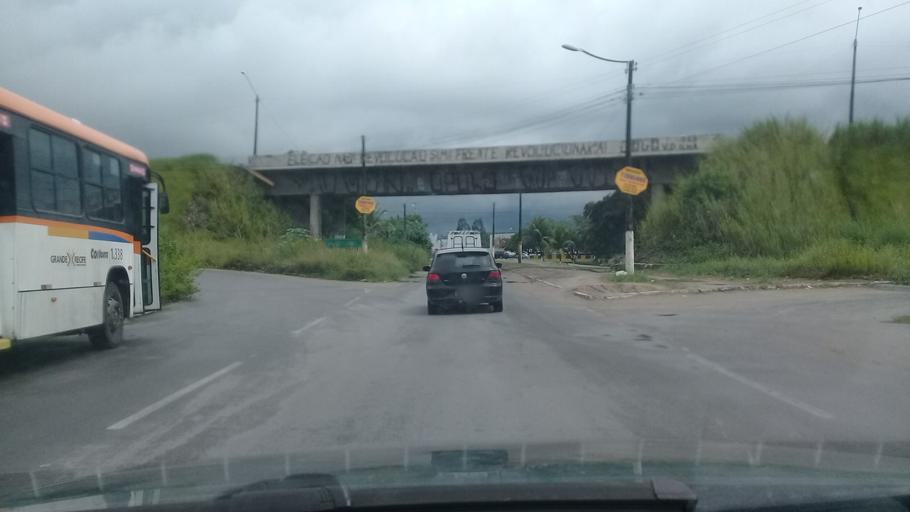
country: BR
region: Pernambuco
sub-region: Igarassu
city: Igarassu
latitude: -7.8332
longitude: -34.9125
